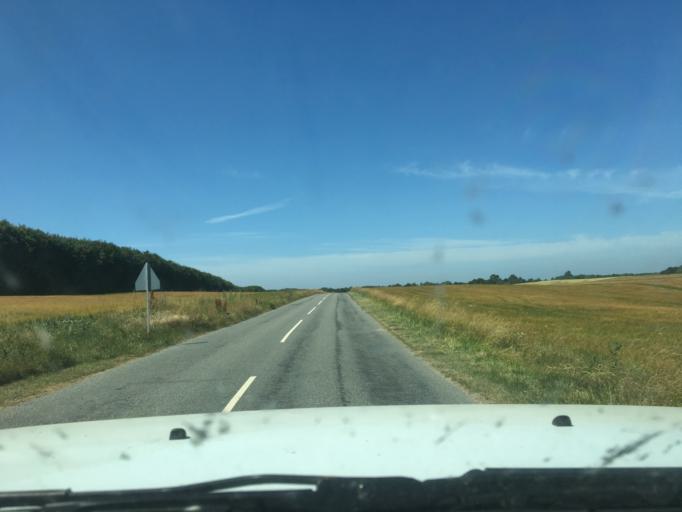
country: DK
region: Central Jutland
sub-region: Favrskov Kommune
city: Ulstrup
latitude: 56.4104
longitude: 9.7858
